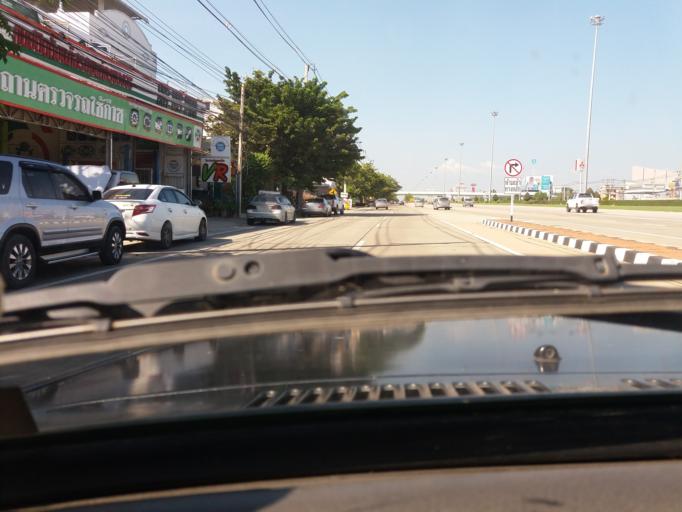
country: TH
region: Suphan Buri
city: Suphan Buri
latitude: 14.4613
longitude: 100.1311
